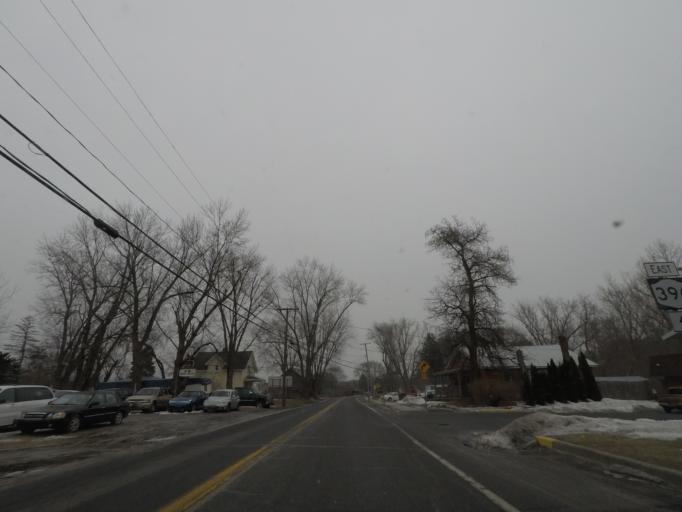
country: US
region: New York
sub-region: Rensselaer County
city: Castleton-on-Hudson
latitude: 42.5482
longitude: -73.8072
